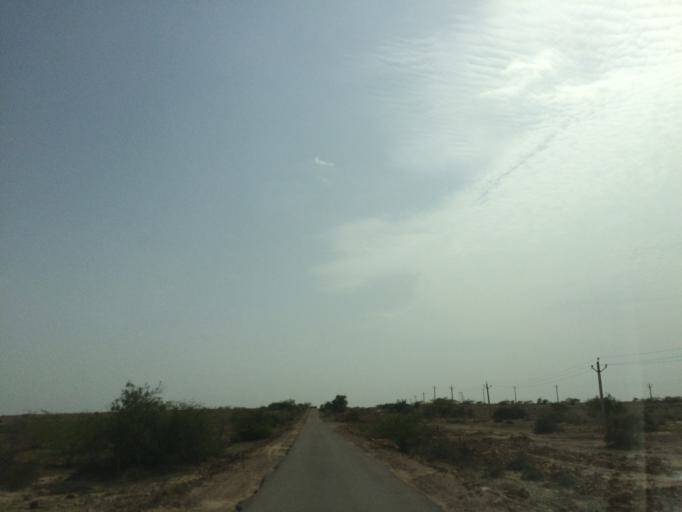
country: IN
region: Rajasthan
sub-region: Jaisalmer
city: Jaisalmer
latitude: 26.8870
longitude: 70.9148
